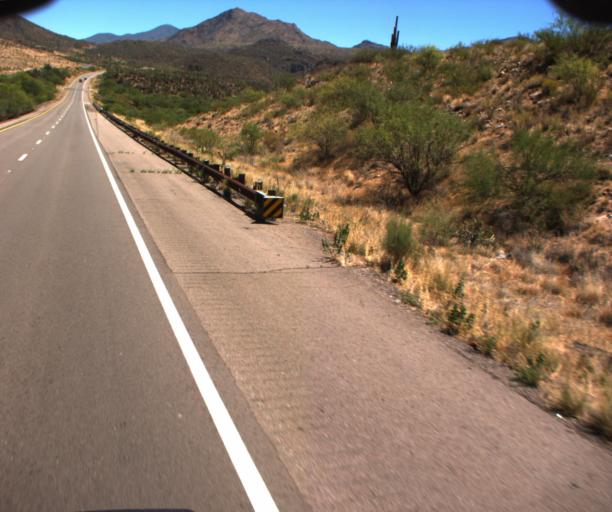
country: US
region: Arizona
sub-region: Maricopa County
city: Rio Verde
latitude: 33.7944
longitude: -111.4934
